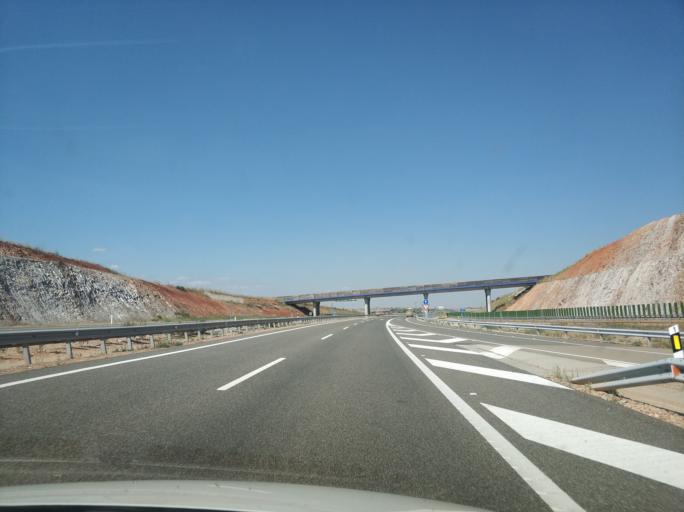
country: ES
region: Castille and Leon
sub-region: Provincia de Zamora
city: Montamarta
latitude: 41.6900
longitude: -5.8025
